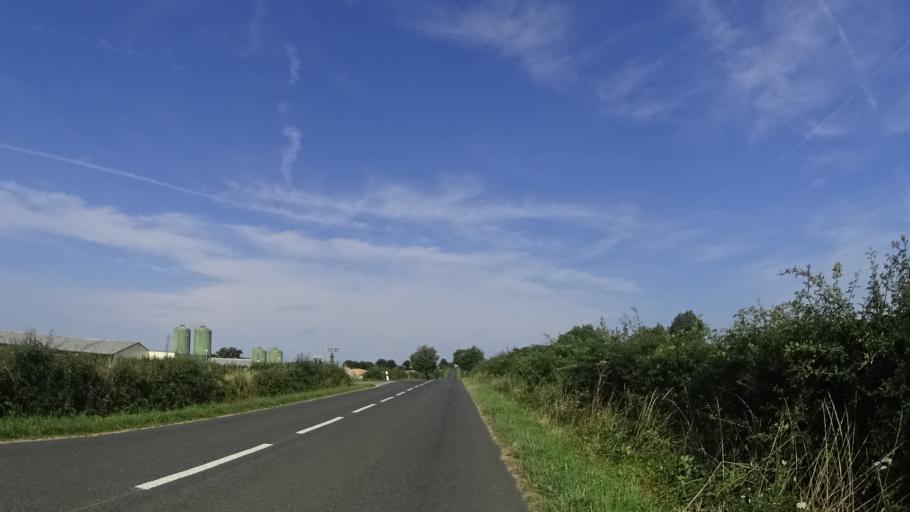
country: FR
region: Pays de la Loire
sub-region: Departement de la Loire-Atlantique
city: Joue-sur-Erdre
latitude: 47.5004
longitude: -1.4568
